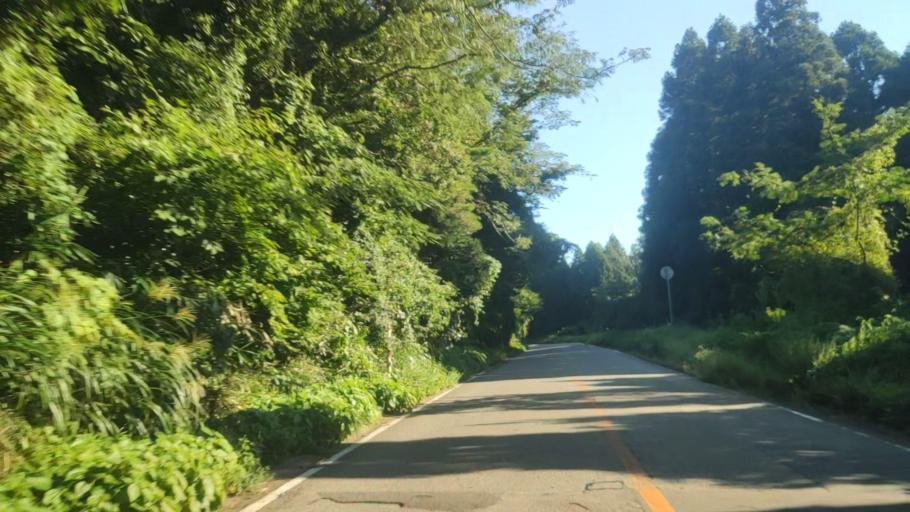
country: JP
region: Ishikawa
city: Nanao
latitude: 37.1057
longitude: 136.9472
